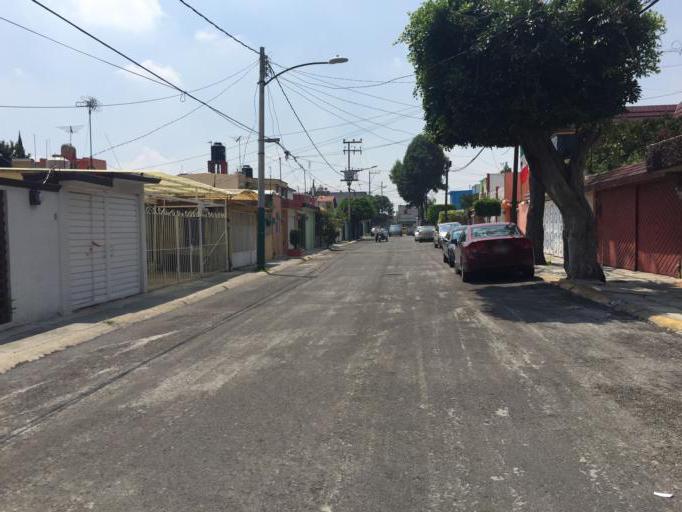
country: MX
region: Mexico
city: Cuautitlan Izcalli
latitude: 19.6515
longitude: -99.2132
